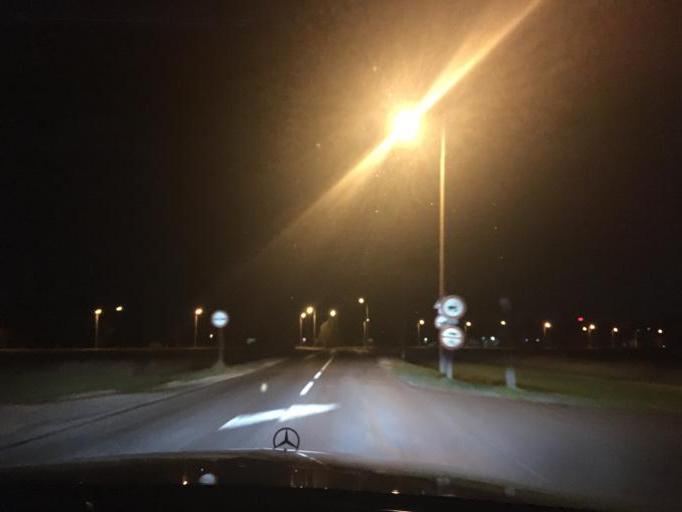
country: HU
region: Hajdu-Bihar
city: Mikepercs
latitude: 47.4844
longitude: 21.6358
